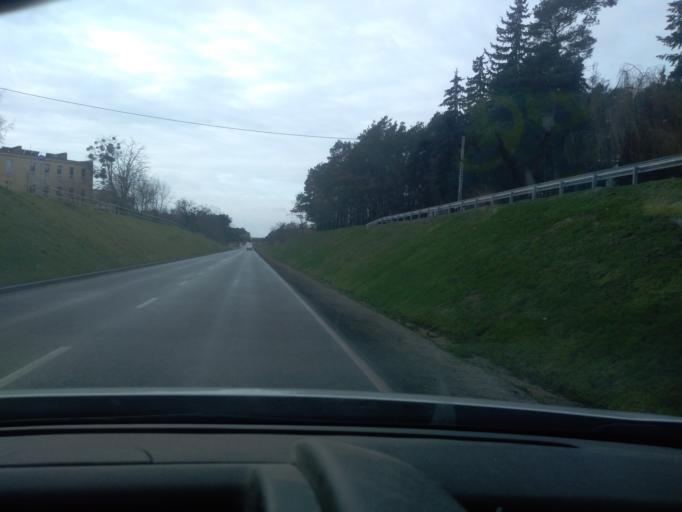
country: PL
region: Greater Poland Voivodeship
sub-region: Powiat obornicki
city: Oborniki
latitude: 52.6545
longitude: 16.8184
